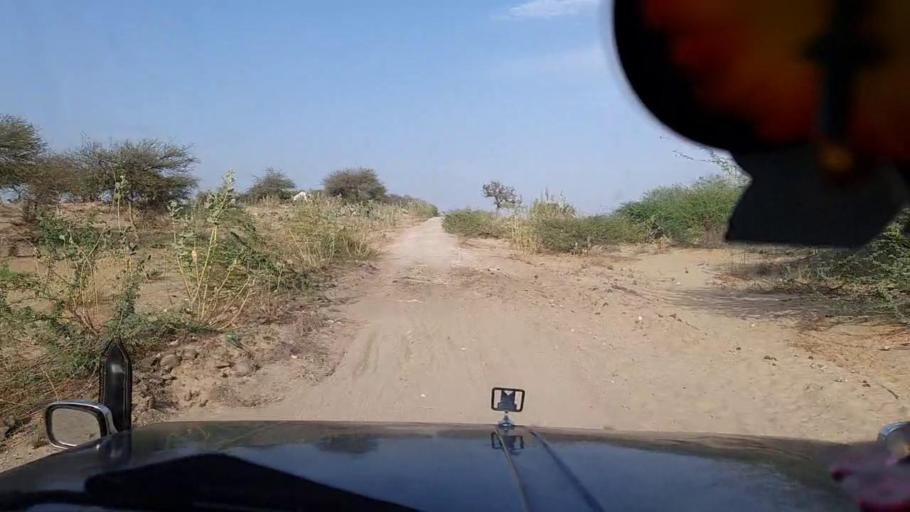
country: PK
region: Sindh
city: Diplo
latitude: 24.5512
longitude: 69.4596
